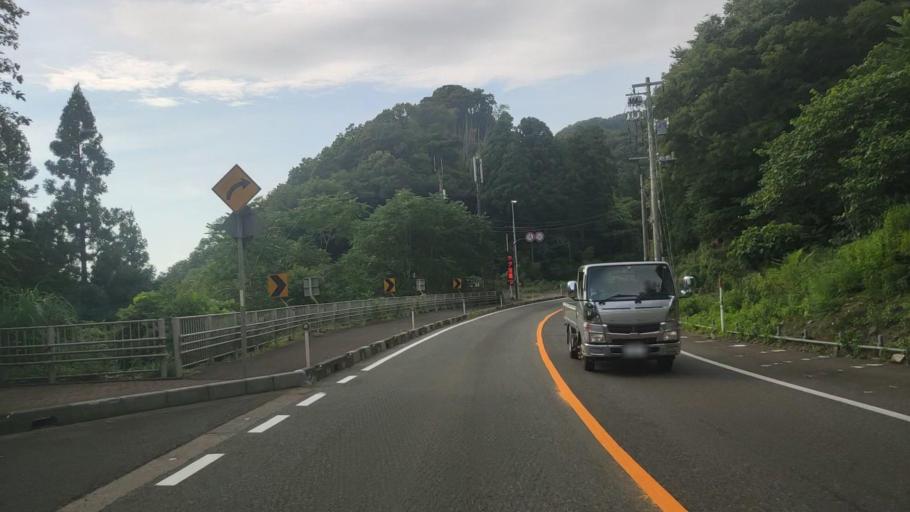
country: JP
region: Fukui
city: Takefu
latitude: 35.7984
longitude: 136.0914
